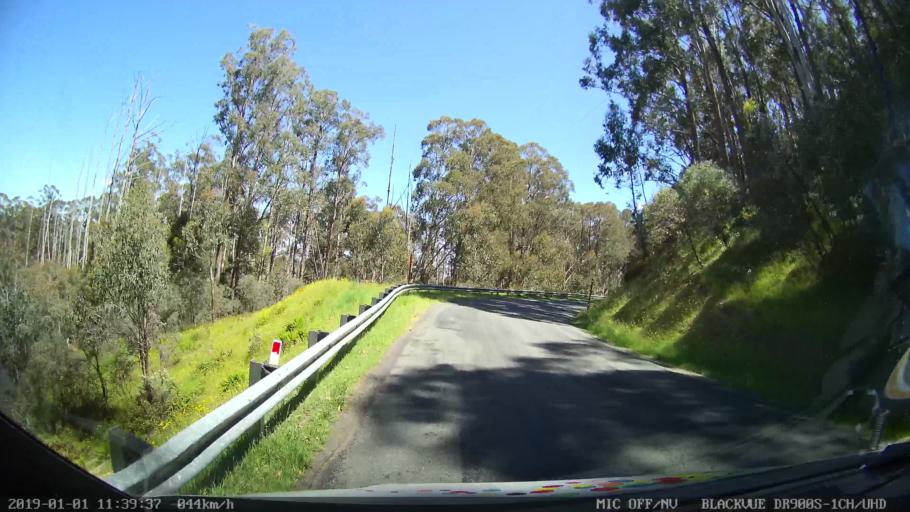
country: AU
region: New South Wales
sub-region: Snowy River
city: Jindabyne
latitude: -35.9254
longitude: 148.3862
